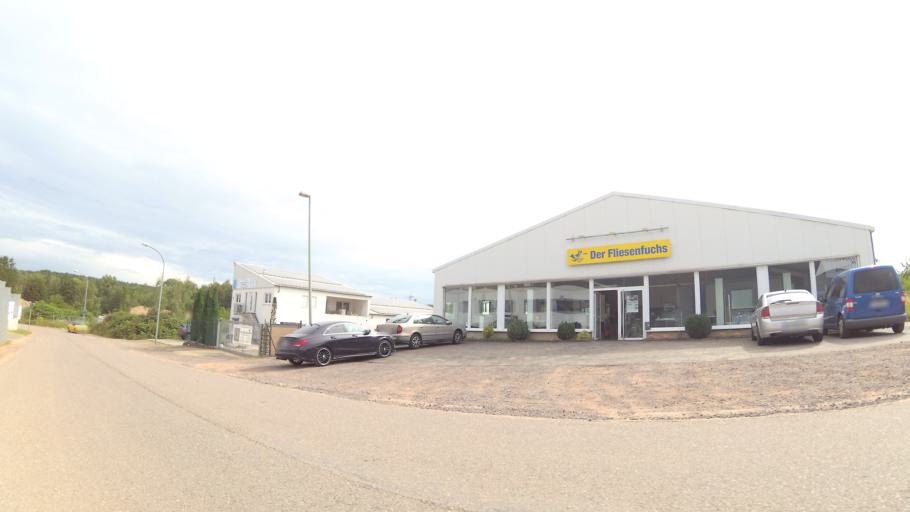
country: DE
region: Saarland
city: Schwalbach
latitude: 49.3254
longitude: 6.8105
